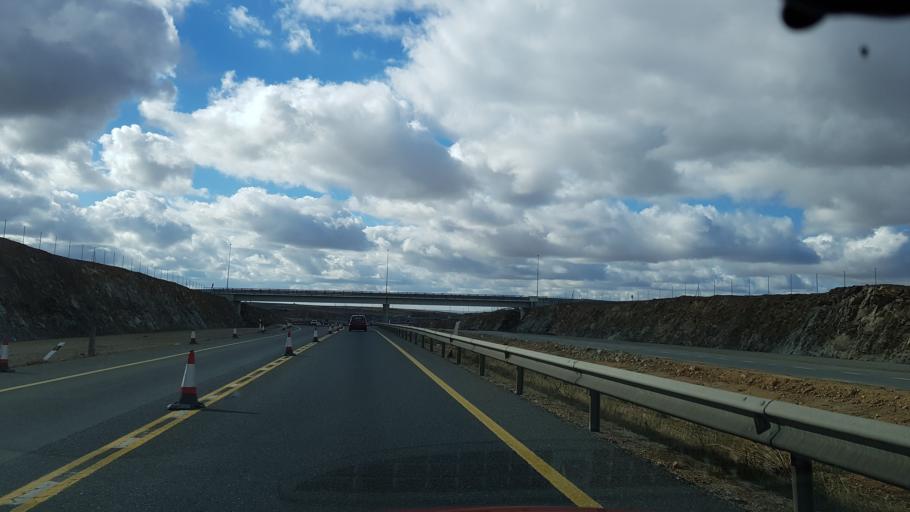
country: ES
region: Castille and Leon
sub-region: Provincia de Segovia
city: Segovia
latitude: 40.9212
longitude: -4.1000
